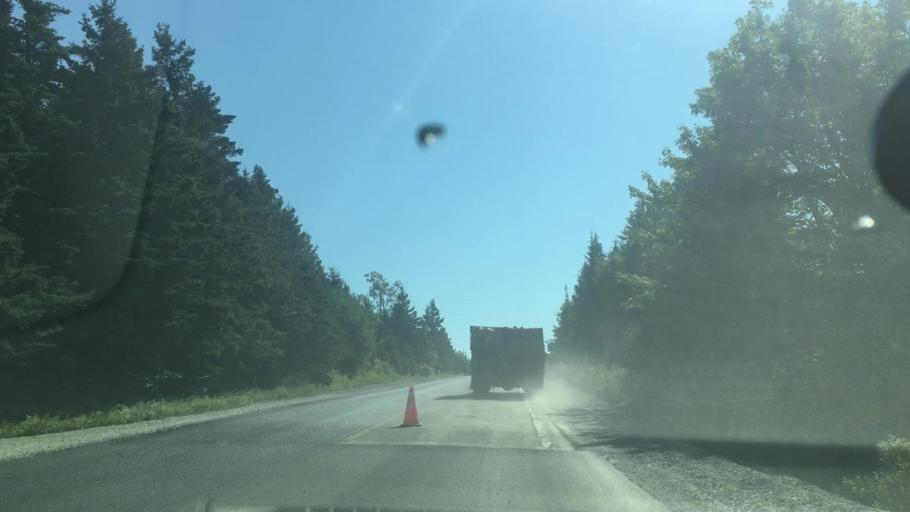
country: CA
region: Nova Scotia
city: New Glasgow
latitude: 44.9064
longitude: -62.4909
